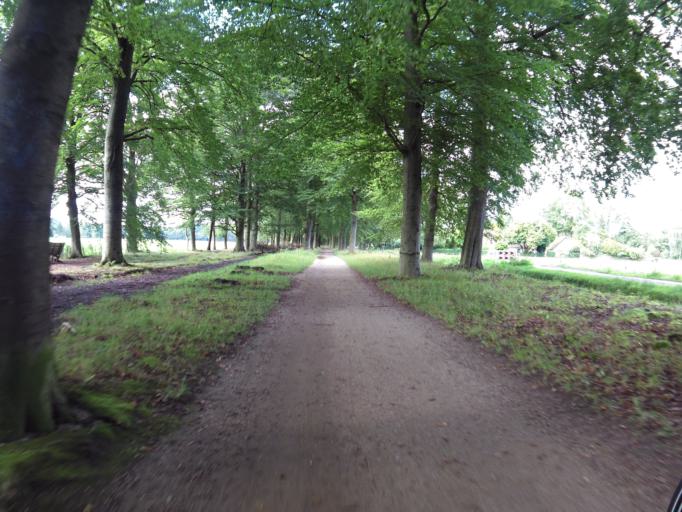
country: NL
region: Utrecht
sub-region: Gemeente Soest
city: Soest
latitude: 52.1684
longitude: 5.2616
